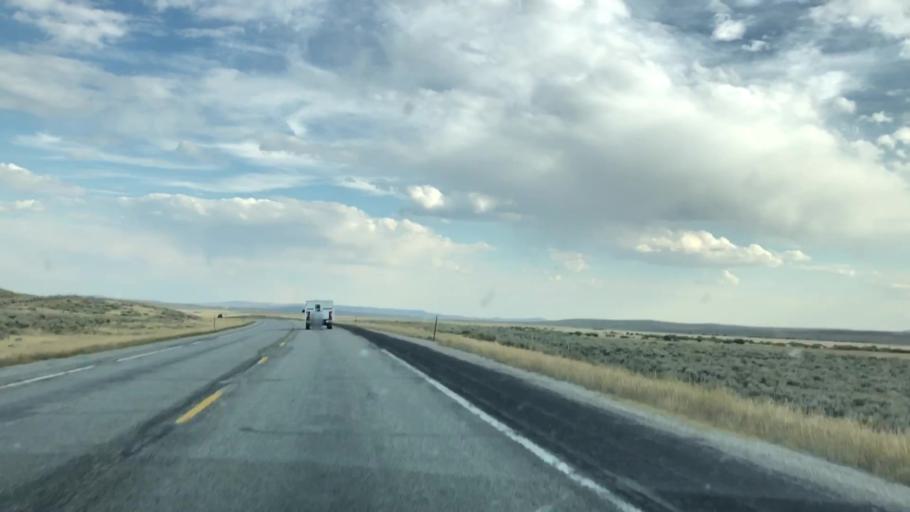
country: US
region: Wyoming
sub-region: Sublette County
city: Pinedale
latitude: 43.0488
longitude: -110.1500
